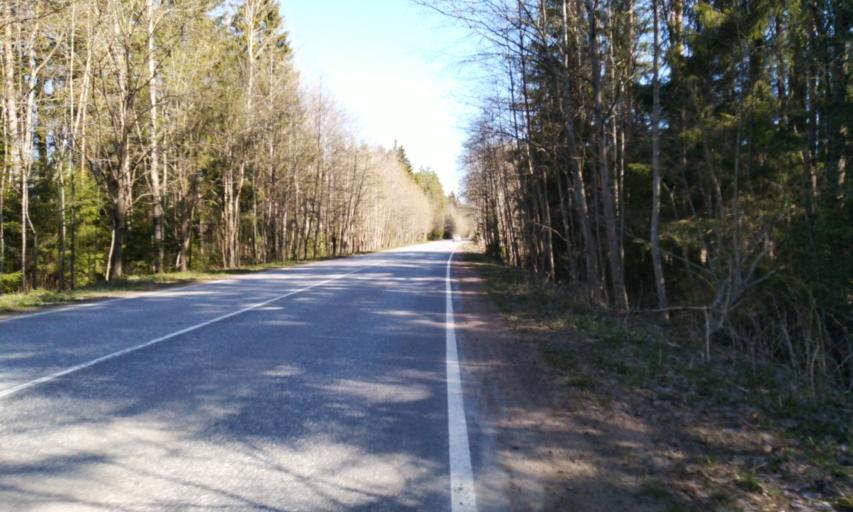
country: RU
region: Leningrad
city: Garbolovo
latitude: 60.3547
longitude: 30.4440
